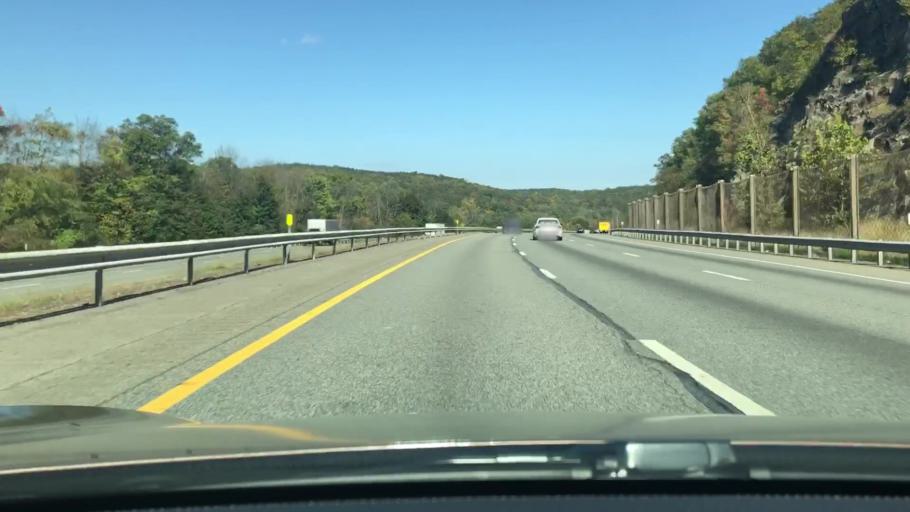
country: US
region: New York
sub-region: Rockland County
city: Sloatsburg
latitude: 41.1696
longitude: -74.1861
